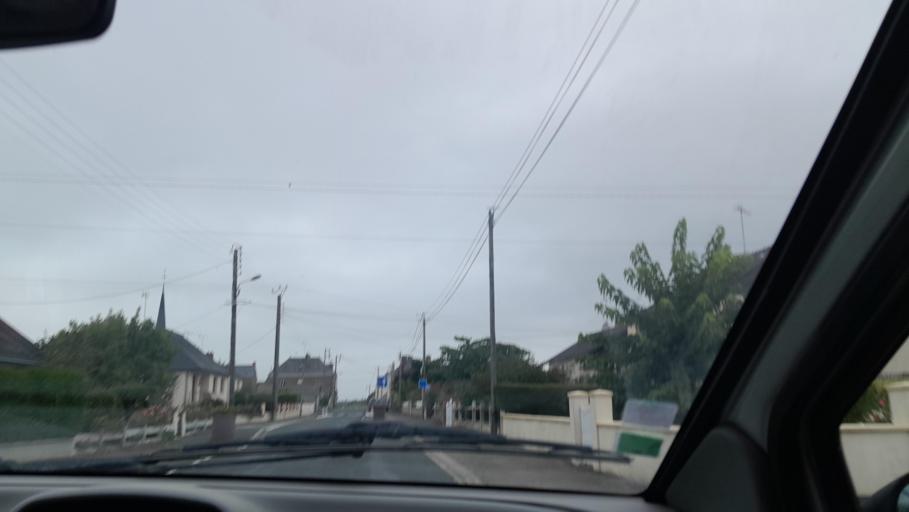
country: FR
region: Pays de la Loire
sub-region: Departement de Maine-et-Loire
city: Pouance
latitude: 47.7154
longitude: -1.1780
